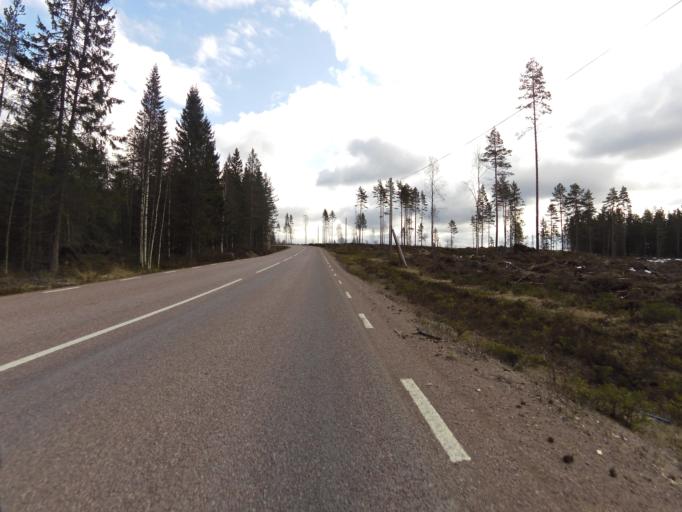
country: SE
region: Dalarna
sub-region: Avesta Kommun
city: Horndal
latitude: 60.3091
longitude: 16.2378
